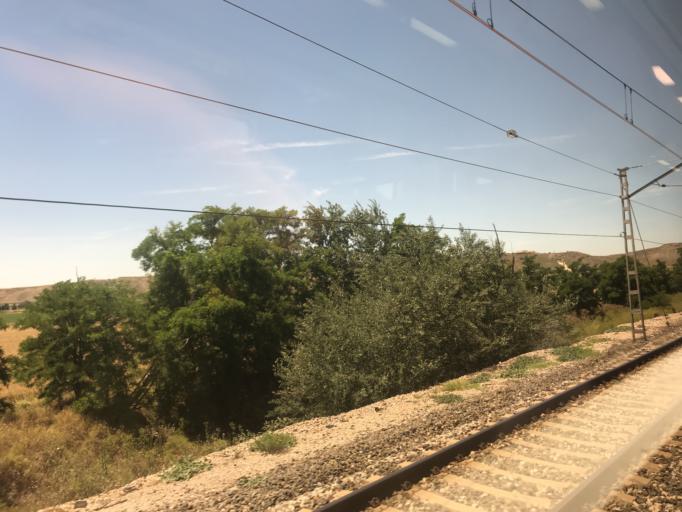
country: ES
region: Madrid
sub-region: Provincia de Madrid
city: Aranjuez
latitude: 40.0550
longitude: -3.6337
